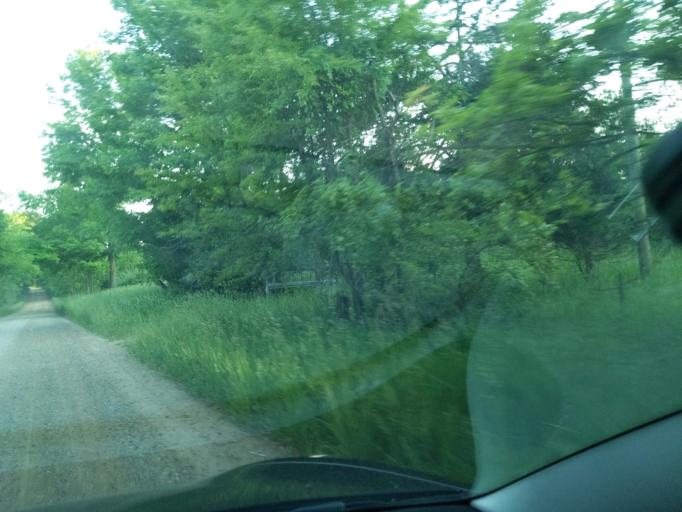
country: US
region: Michigan
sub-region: Barry County
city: Nashville
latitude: 42.5363
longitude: -85.1133
